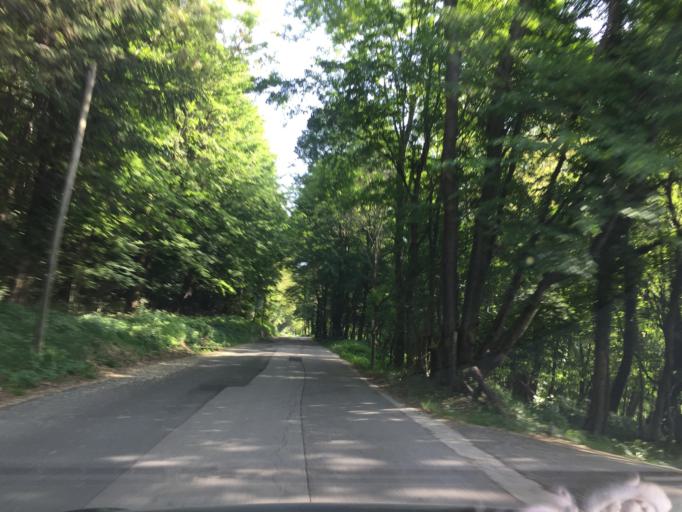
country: HR
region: Primorsko-Goranska
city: Klana
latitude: 45.4612
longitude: 14.3784
